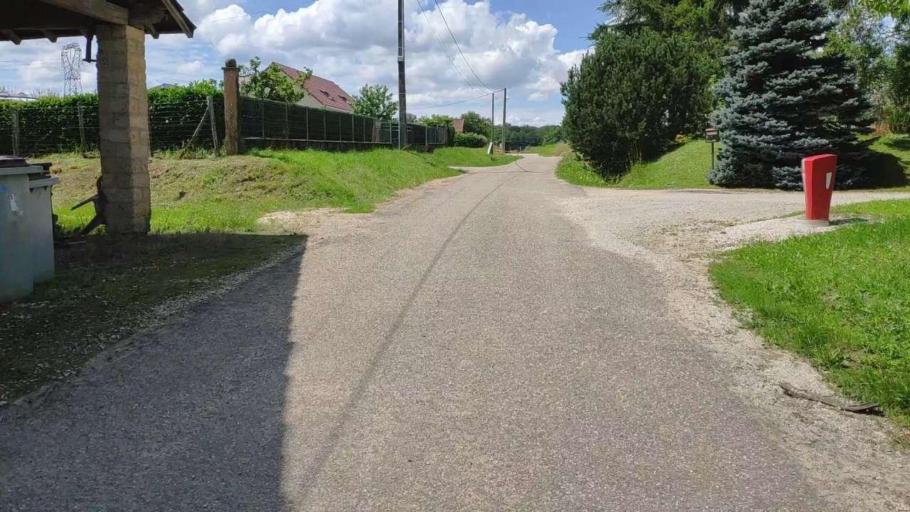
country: FR
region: Franche-Comte
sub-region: Departement du Jura
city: Chaussin
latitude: 46.8893
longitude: 5.4965
